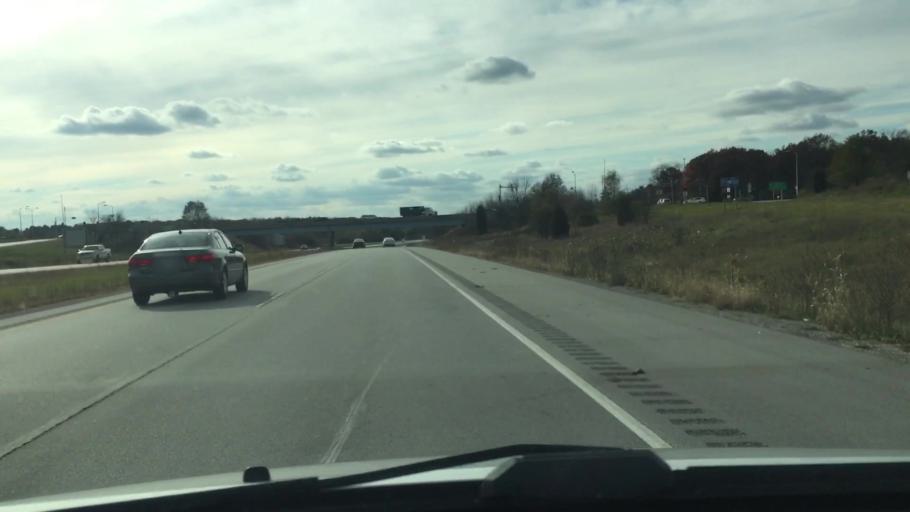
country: US
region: Wisconsin
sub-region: Waukesha County
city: Hartland
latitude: 43.1065
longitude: -88.3601
